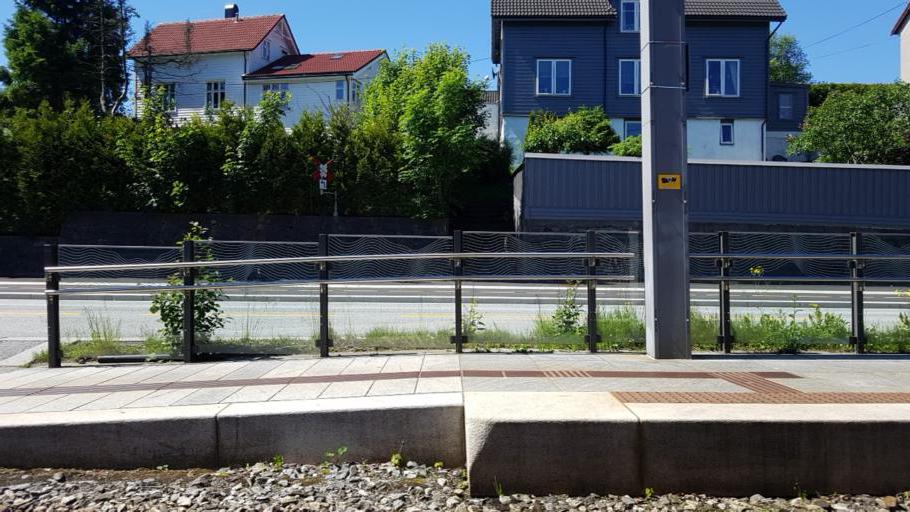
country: NO
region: Hordaland
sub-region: Bergen
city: Sandsli
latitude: 60.3260
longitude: 5.3464
